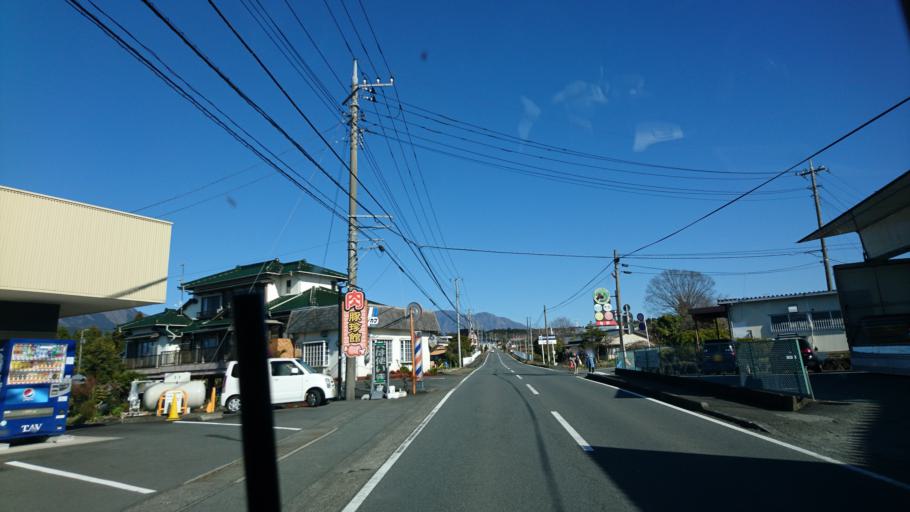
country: JP
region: Shizuoka
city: Fujinomiya
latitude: 35.2812
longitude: 138.6039
